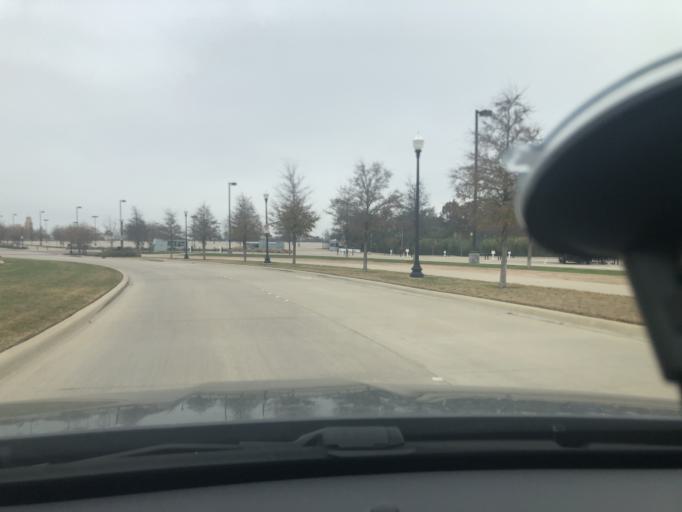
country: US
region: Texas
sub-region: Tarrant County
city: Westworth
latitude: 32.7366
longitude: -97.3680
